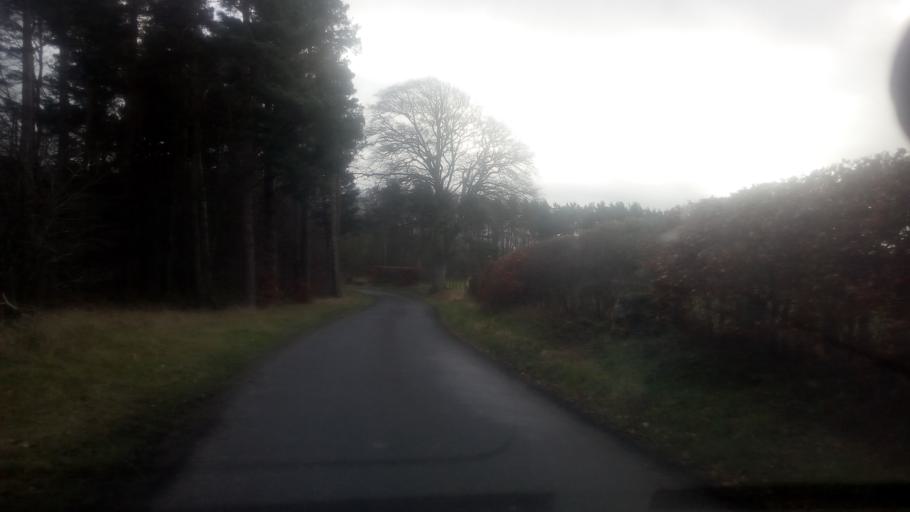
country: GB
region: Scotland
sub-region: The Scottish Borders
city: Kelso
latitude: 55.5450
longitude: -2.4875
